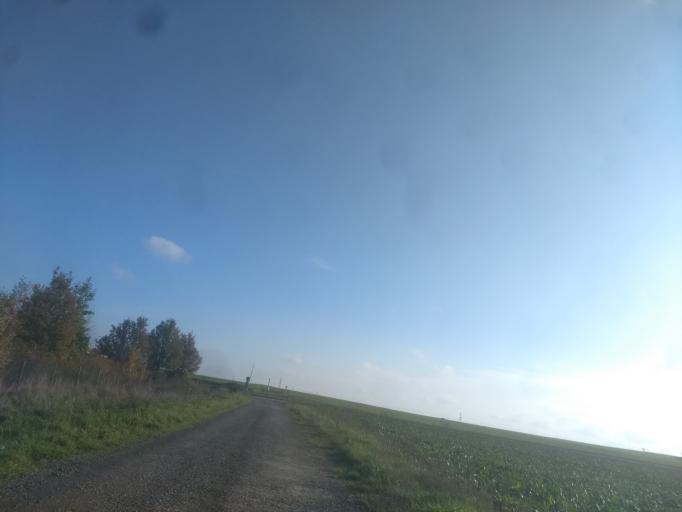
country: FR
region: Nord-Pas-de-Calais
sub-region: Departement du Pas-de-Calais
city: Tilloy-les-Mofflaines
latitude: 50.2726
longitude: 2.8076
